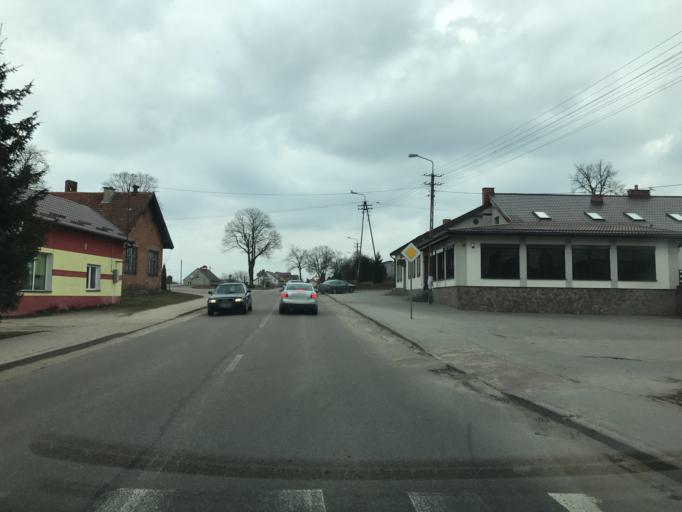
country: PL
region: Warmian-Masurian Voivodeship
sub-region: Powiat dzialdowski
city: Dzialdowo
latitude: 53.2721
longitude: 20.1450
